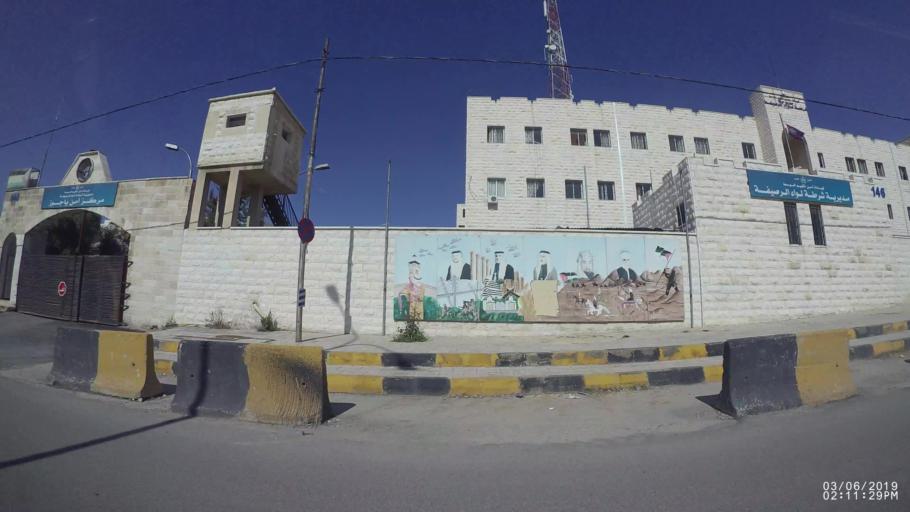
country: JO
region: Zarqa
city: Russeifa
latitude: 32.0292
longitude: 36.0500
